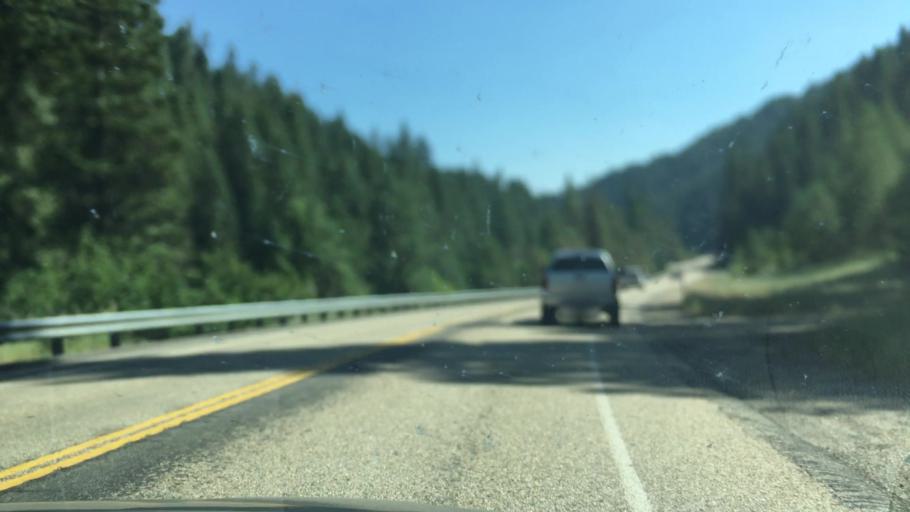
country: US
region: Idaho
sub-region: Valley County
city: Cascade
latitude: 44.1641
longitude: -116.1181
